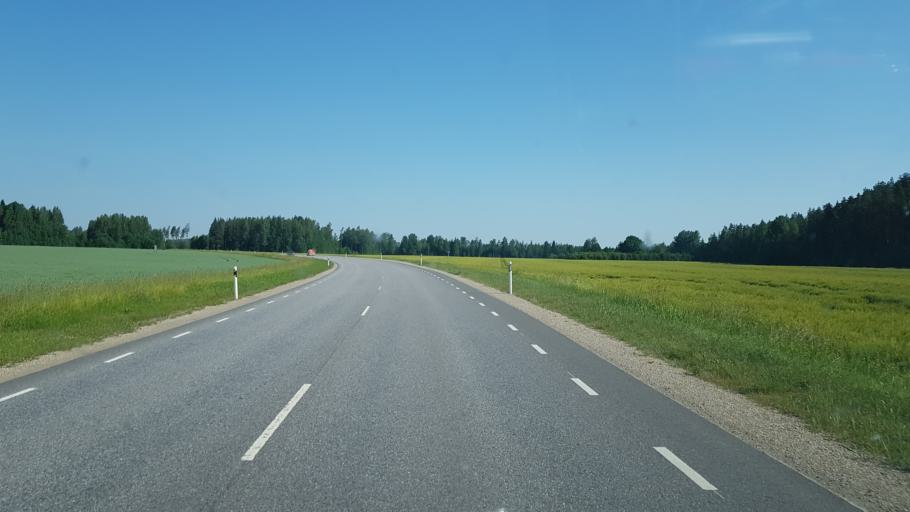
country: EE
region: Polvamaa
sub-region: Polva linn
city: Polva
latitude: 58.1284
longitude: 26.9561
